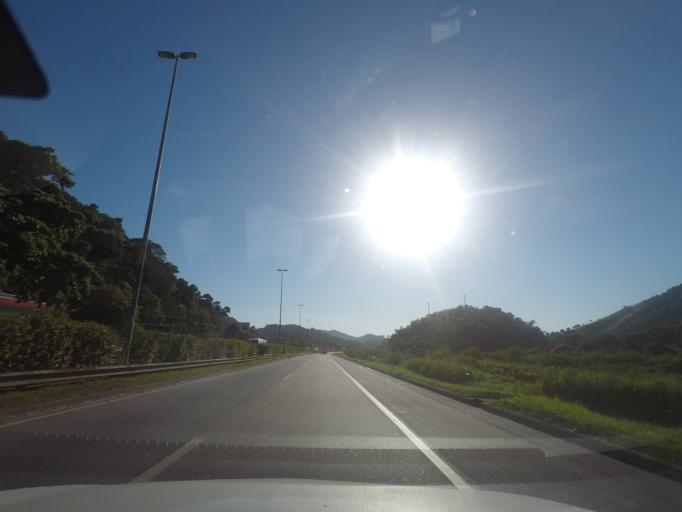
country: BR
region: Rio de Janeiro
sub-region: Petropolis
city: Petropolis
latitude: -22.6537
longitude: -43.1486
